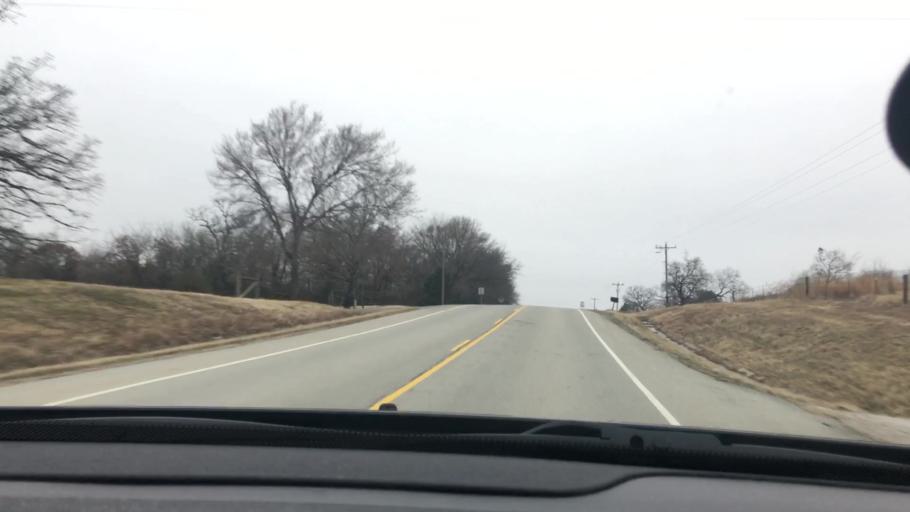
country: US
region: Oklahoma
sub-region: Coal County
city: Coalgate
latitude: 34.5055
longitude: -96.3673
